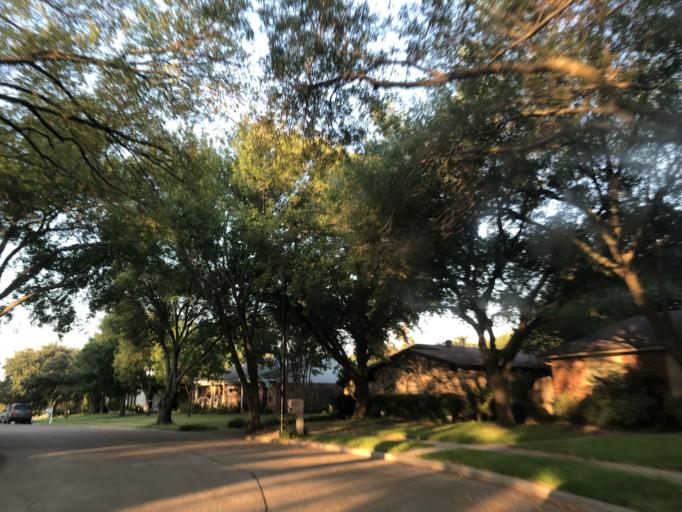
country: US
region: Texas
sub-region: Dallas County
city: Sunnyvale
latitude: 32.8414
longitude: -96.5756
